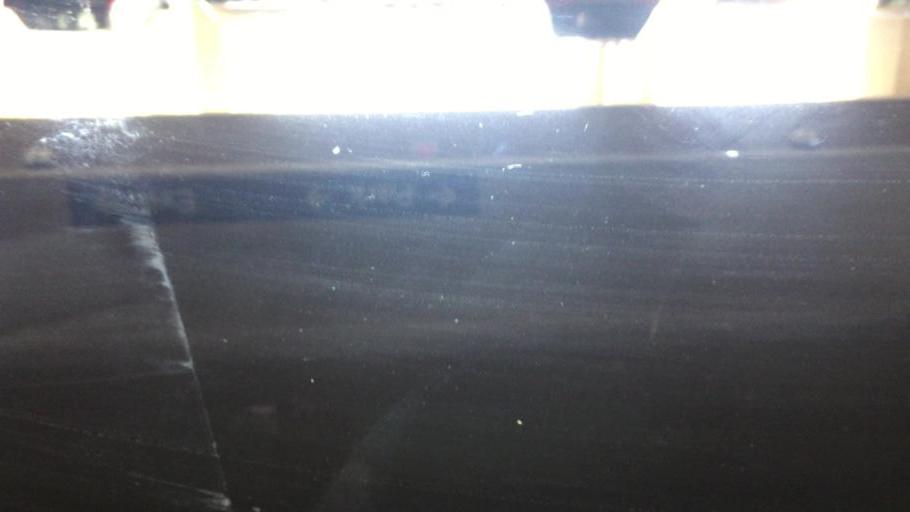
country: US
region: California
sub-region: Orange County
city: Irvine
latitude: 33.6473
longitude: -117.8369
